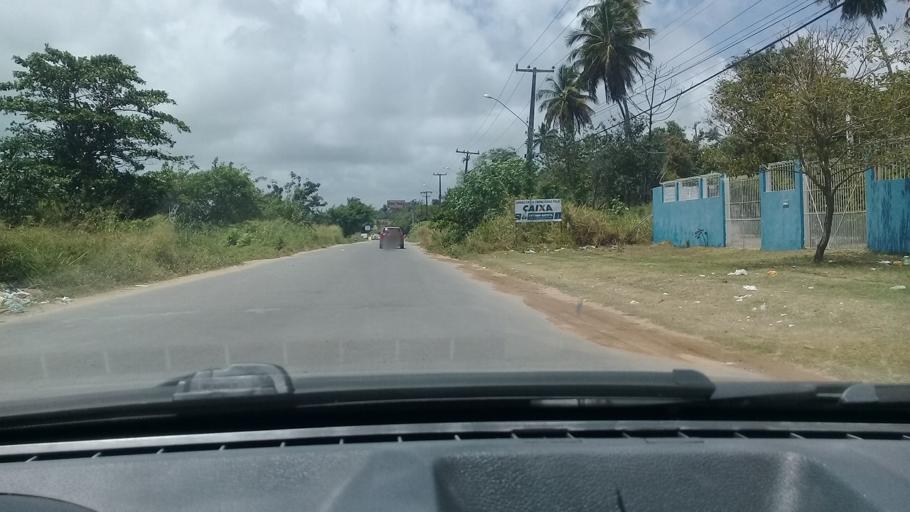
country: BR
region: Pernambuco
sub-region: Itamaraca
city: Itamaraca
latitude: -7.7903
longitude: -34.8410
